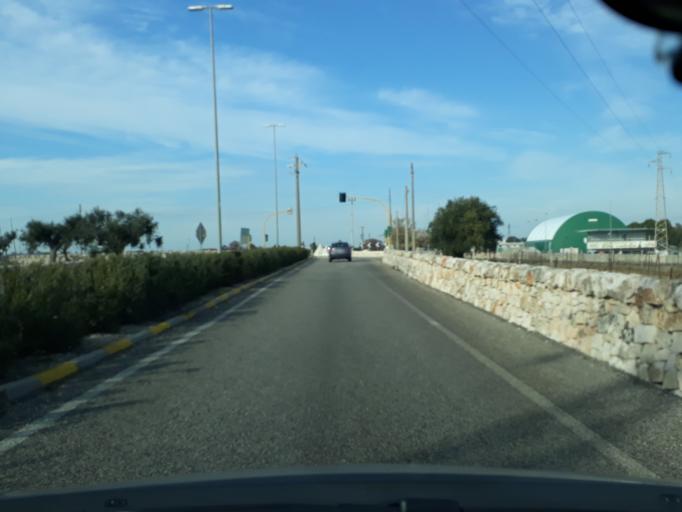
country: IT
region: Apulia
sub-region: Provincia di Bari
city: Locorotondo
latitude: 40.7553
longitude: 17.3437
